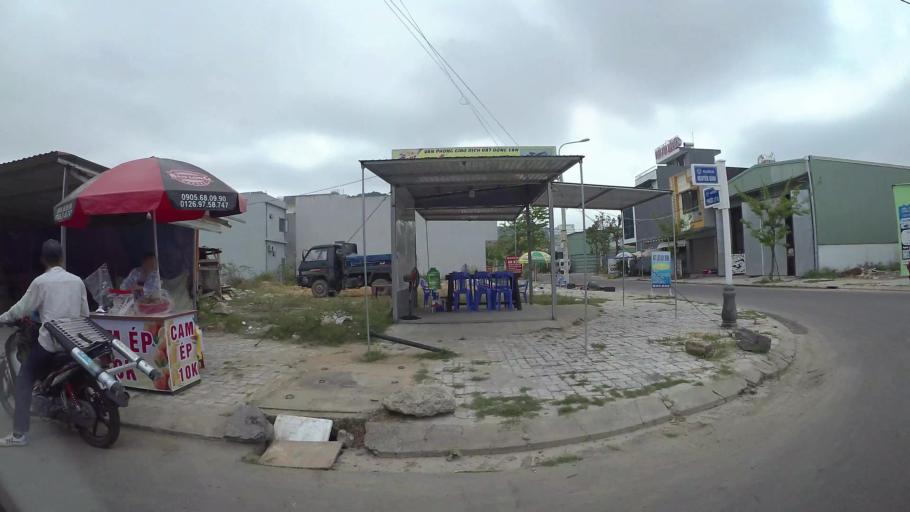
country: VN
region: Da Nang
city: Lien Chieu
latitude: 16.0465
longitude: 108.1691
